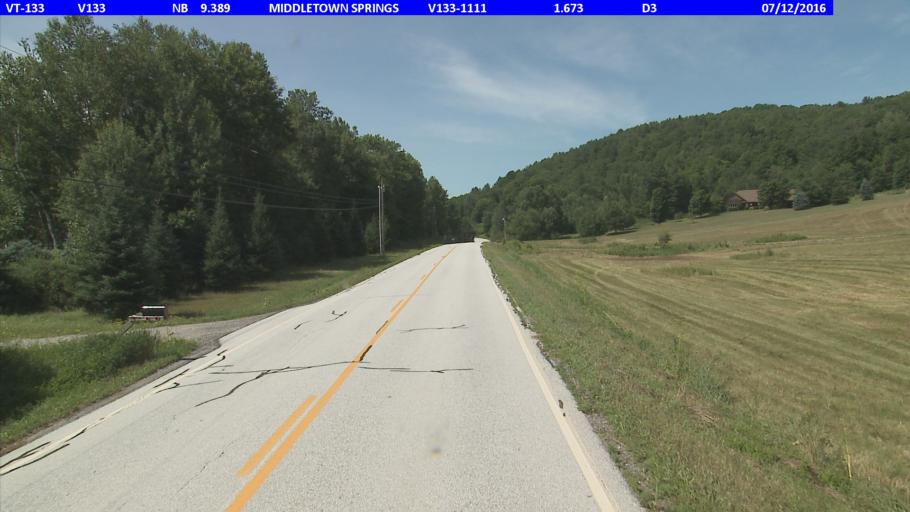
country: US
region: Vermont
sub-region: Rutland County
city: Poultney
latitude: 43.4592
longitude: -73.1105
